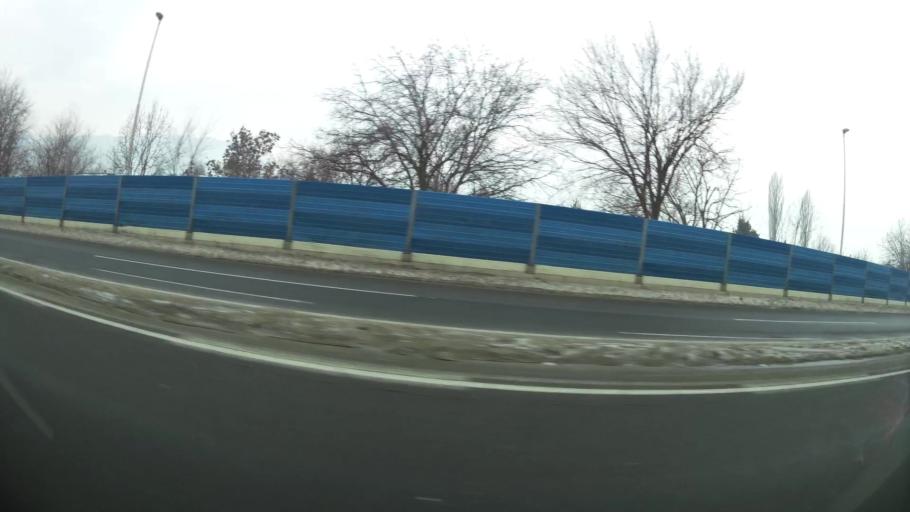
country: MK
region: Saraj
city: Saraj
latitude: 42.0081
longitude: 21.3287
